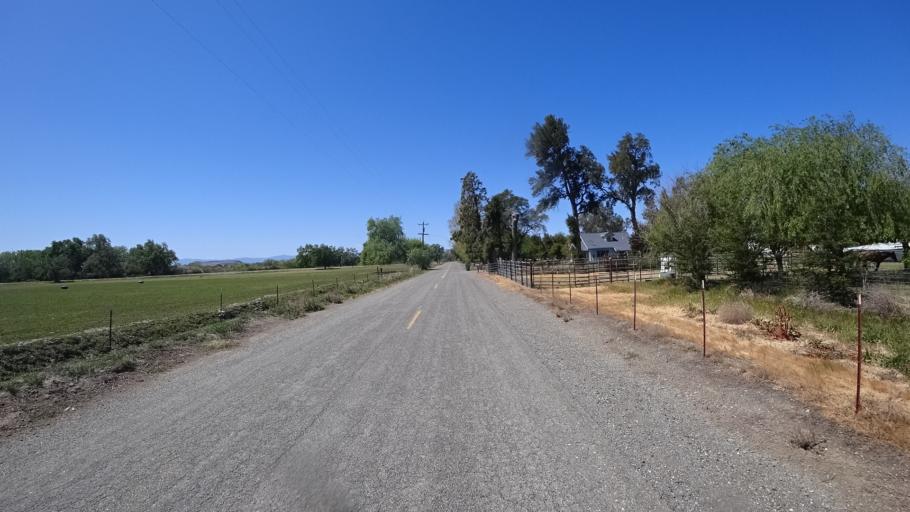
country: US
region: California
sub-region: Glenn County
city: Orland
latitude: 39.7952
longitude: -122.2473
